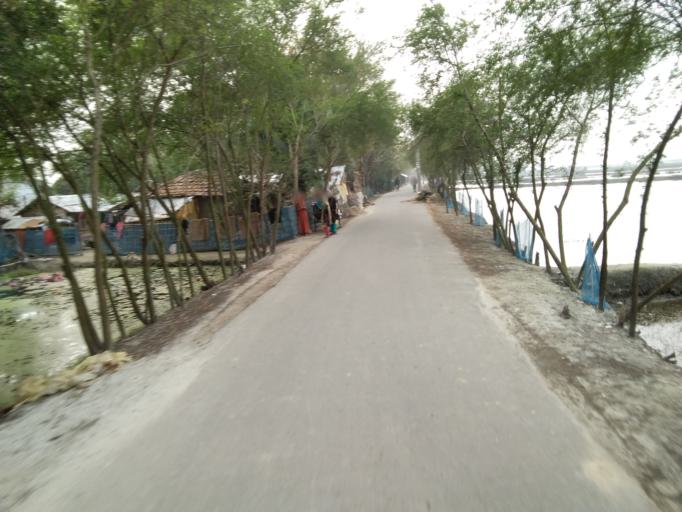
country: BD
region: Khulna
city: Satkhira
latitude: 22.5848
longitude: 89.0622
